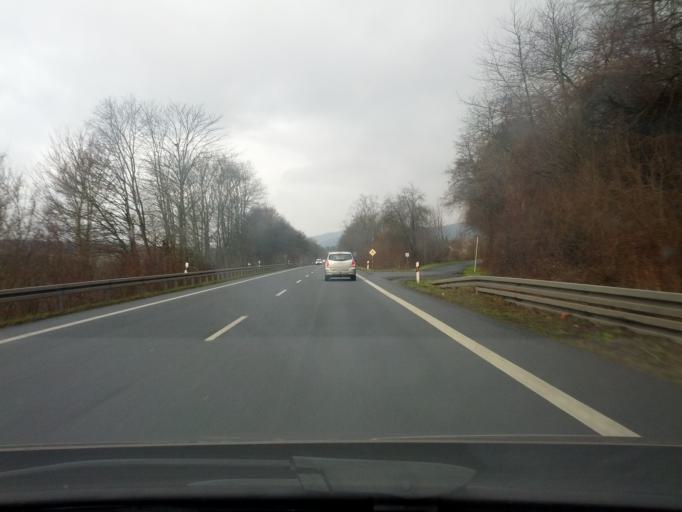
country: DE
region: Hesse
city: Witzenhausen
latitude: 51.3721
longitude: 9.8065
